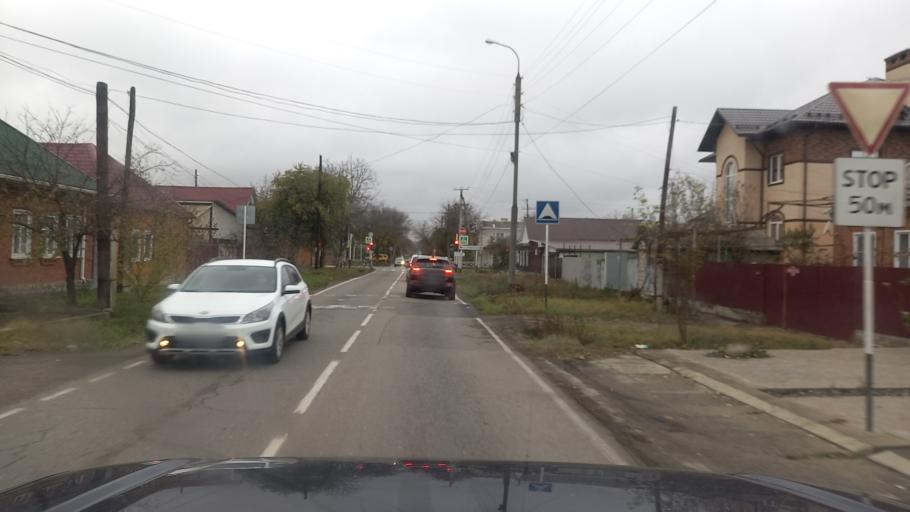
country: RU
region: Adygeya
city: Maykop
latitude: 44.6047
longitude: 40.0801
